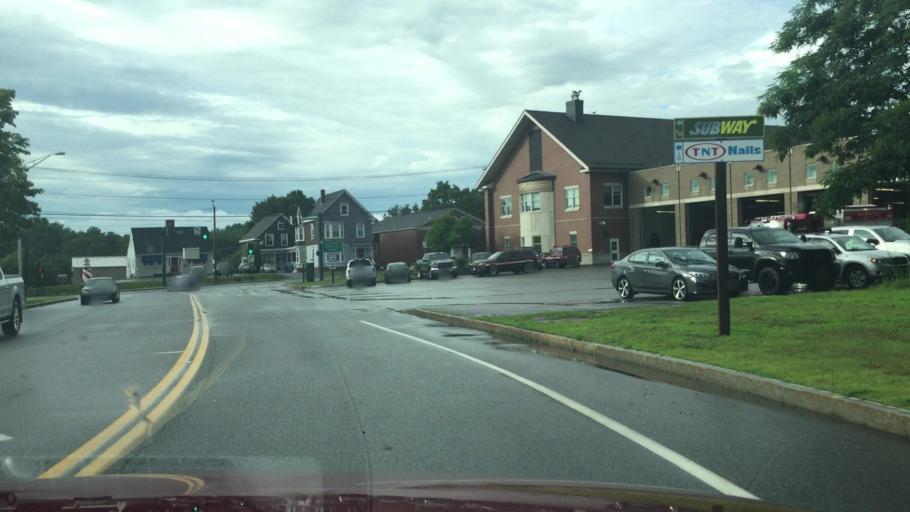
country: US
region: Maine
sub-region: Cumberland County
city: Westbrook
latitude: 43.6784
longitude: -70.3542
